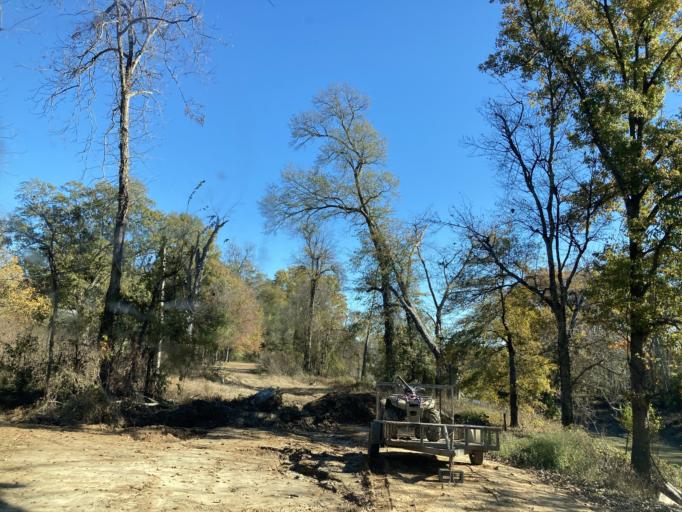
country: US
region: Mississippi
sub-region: Sharkey County
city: Rolling Fork
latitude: 32.8180
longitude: -90.7108
